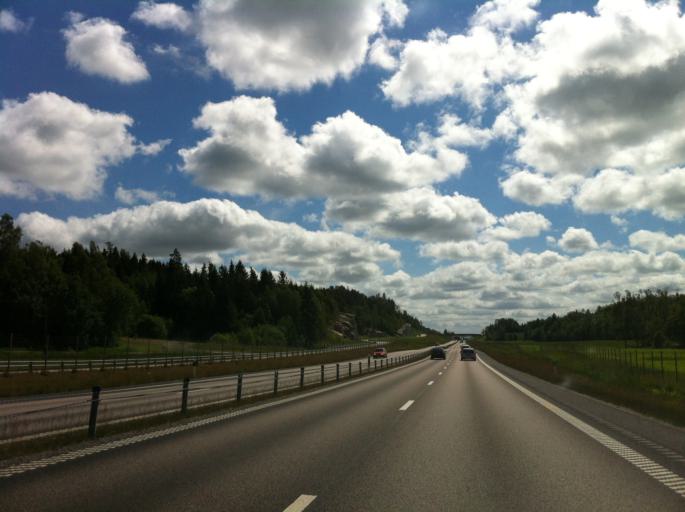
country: SE
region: Vaestra Goetaland
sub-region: Lilla Edets Kommun
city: Lilla Edet
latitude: 58.1783
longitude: 12.1407
